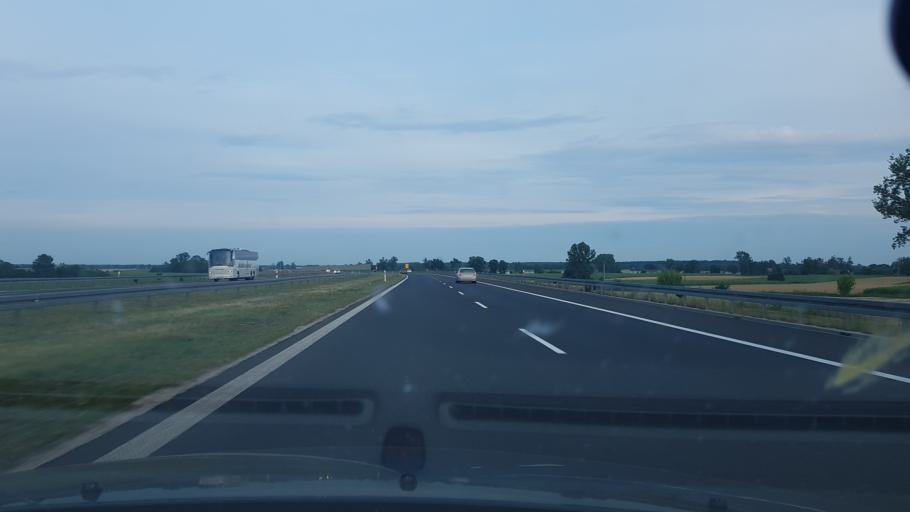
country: PL
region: Lodz Voivodeship
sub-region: Powiat kutnowski
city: Lanieta
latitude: 52.3896
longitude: 19.2924
